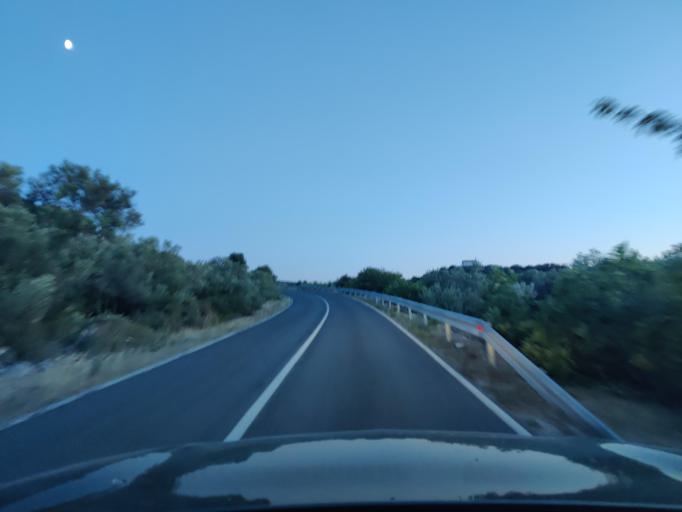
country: HR
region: Sibensko-Kniniska
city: Murter
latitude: 43.8176
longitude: 15.6003
